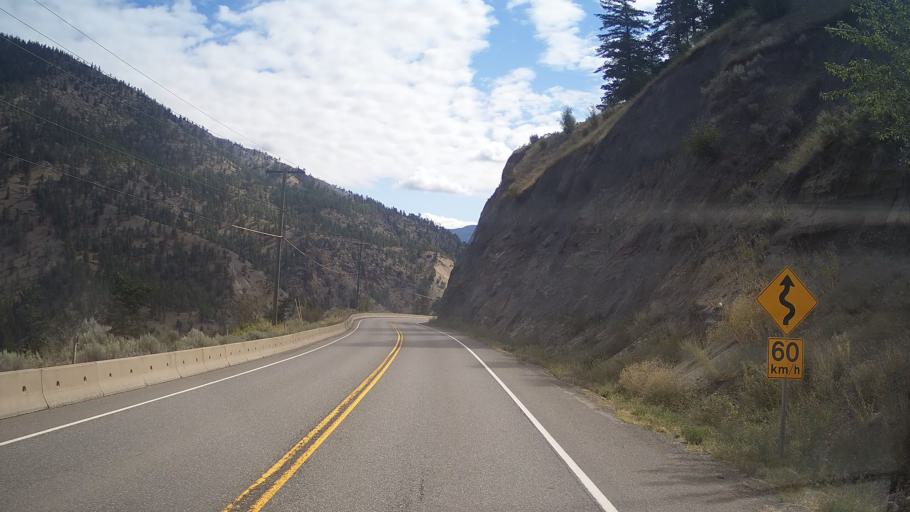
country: CA
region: British Columbia
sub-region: Thompson-Nicola Regional District
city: Ashcroft
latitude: 50.2571
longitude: -121.4683
